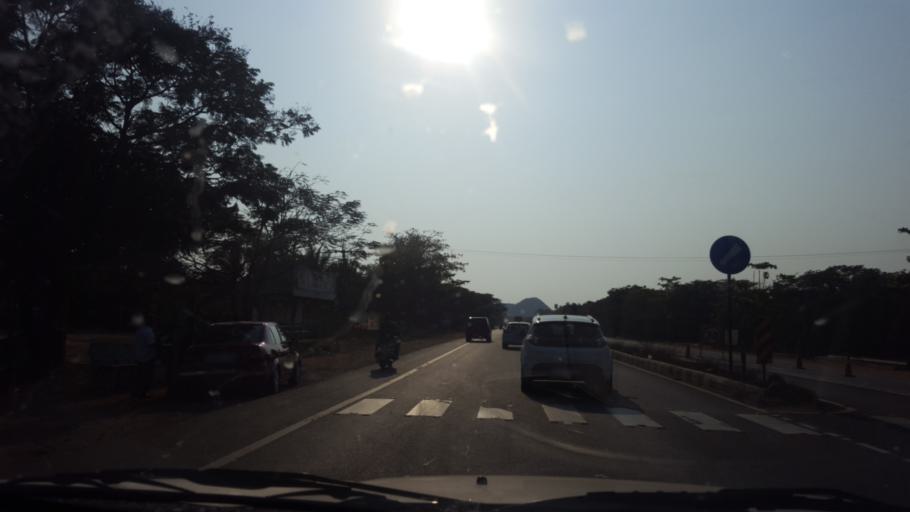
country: IN
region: Andhra Pradesh
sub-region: Vishakhapatnam
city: Etikoppaka
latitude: 17.3952
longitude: 82.6677
